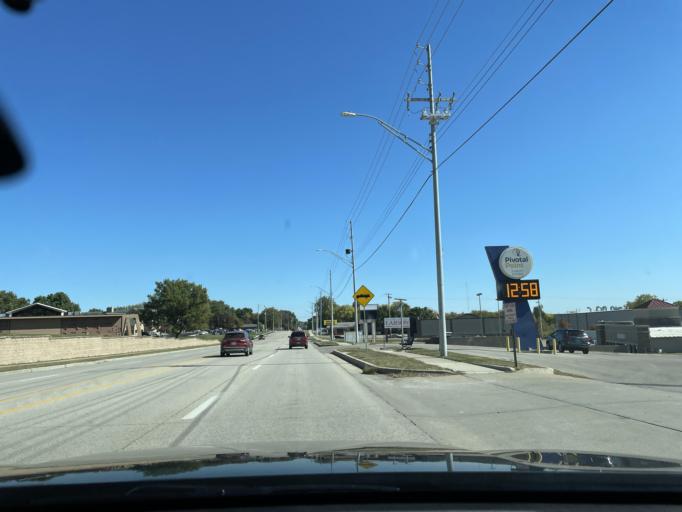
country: US
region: Missouri
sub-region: Andrew County
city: Country Club Village
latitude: 39.7797
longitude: -94.7805
